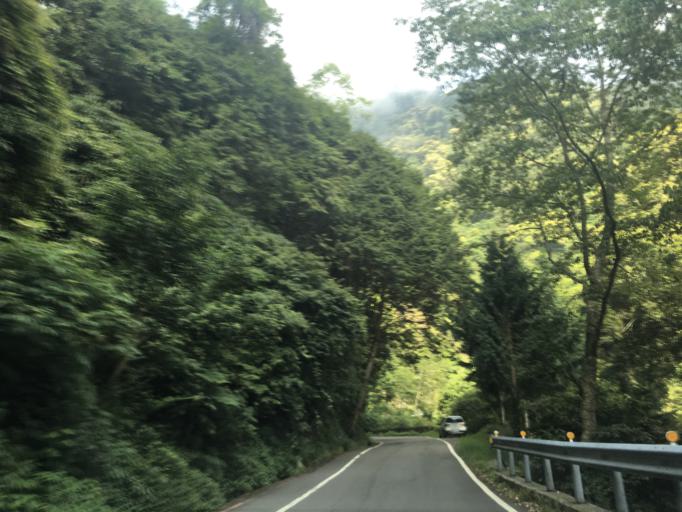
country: TW
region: Taiwan
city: Fengyuan
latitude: 24.2344
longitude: 120.9664
